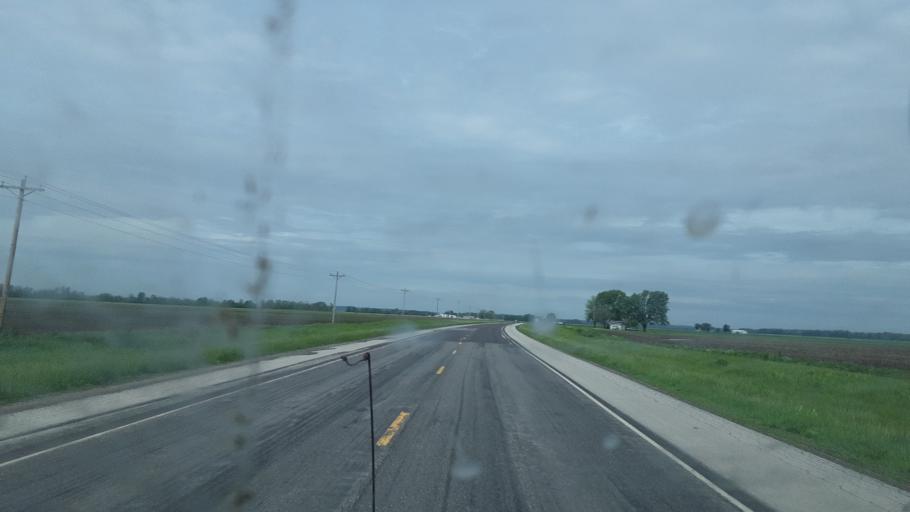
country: US
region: Illinois
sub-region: Hancock County
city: Warsaw
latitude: 40.3759
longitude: -91.4892
